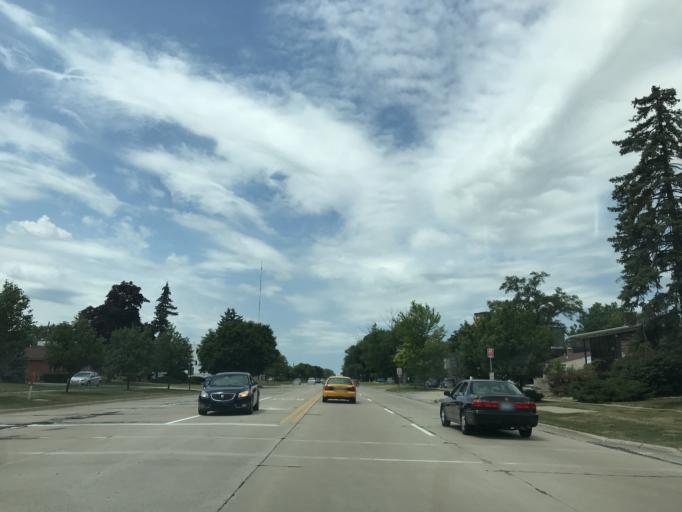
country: US
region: Michigan
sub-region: Oakland County
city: Southfield
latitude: 42.4732
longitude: -83.2309
